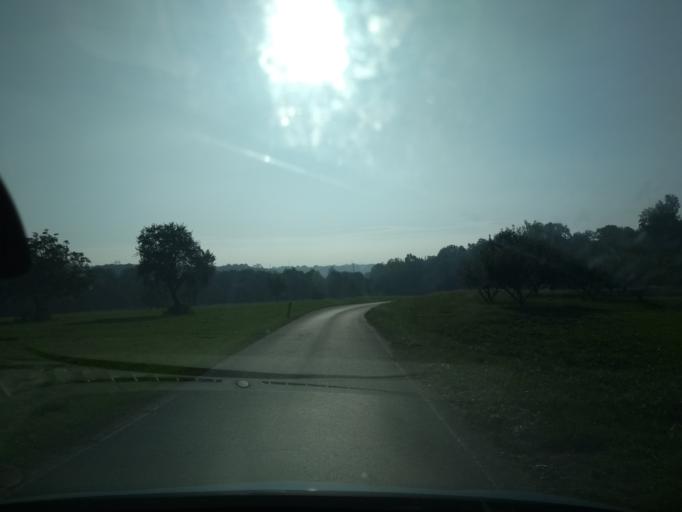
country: IT
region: Piedmont
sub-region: Provincia di Torino
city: Vallo Torinese
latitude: 45.2232
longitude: 7.5008
